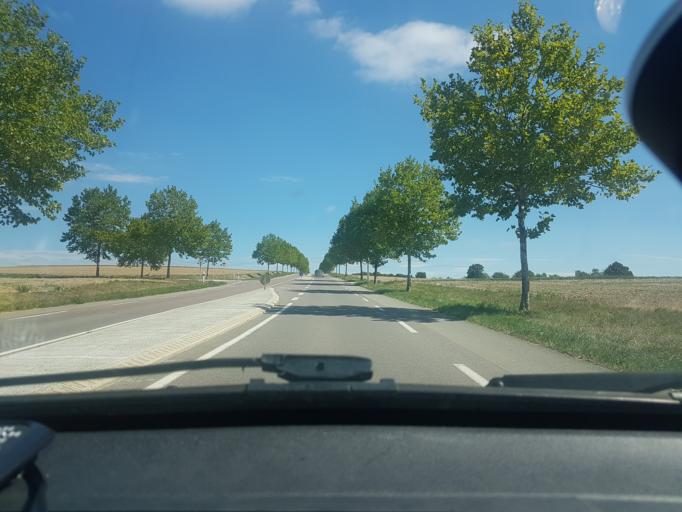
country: FR
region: Bourgogne
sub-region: Departement de la Cote-d'Or
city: Belleneuve
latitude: 47.3822
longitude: 5.2614
